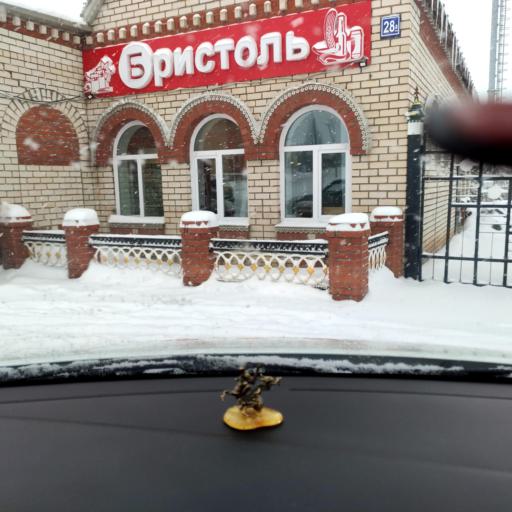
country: RU
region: Tatarstan
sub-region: Arskiy Rayon
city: Arsk
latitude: 56.0993
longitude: 49.8757
